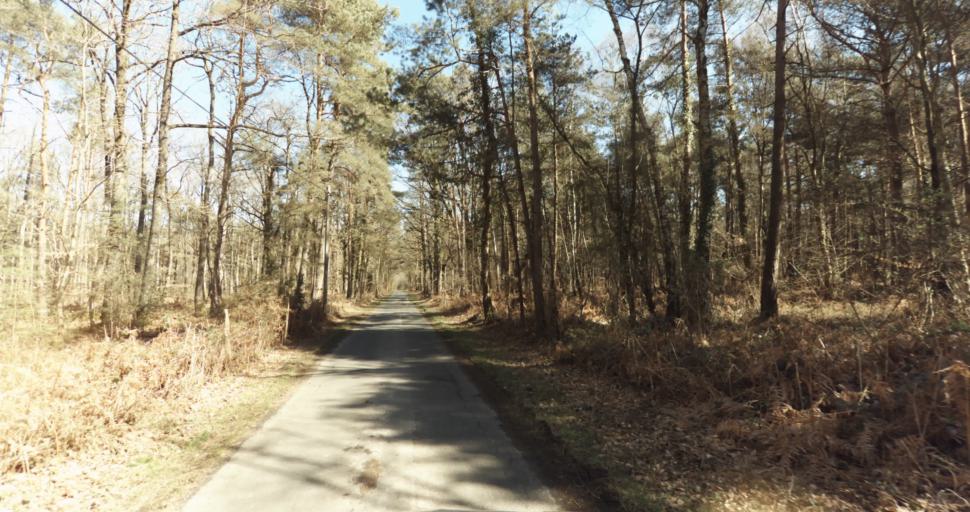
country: FR
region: Lower Normandy
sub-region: Departement du Calvados
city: Livarot
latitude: 48.9743
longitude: 0.0787
